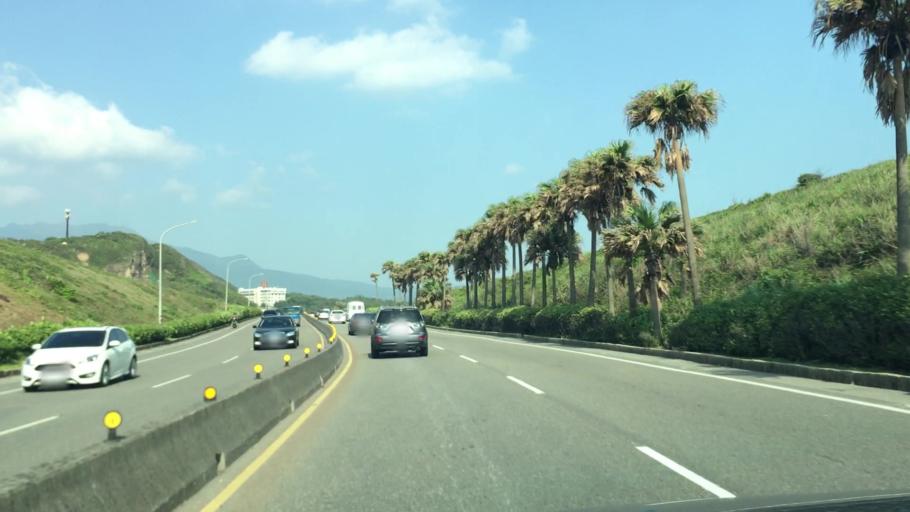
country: TW
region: Taiwan
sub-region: Keelung
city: Keelung
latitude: 25.2052
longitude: 121.6657
